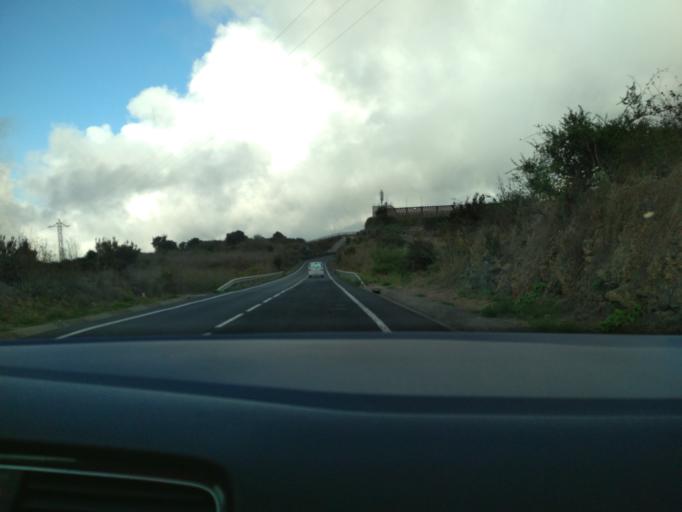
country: ES
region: Canary Islands
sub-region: Provincia de Santa Cruz de Tenerife
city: Santiago del Teide
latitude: 28.3294
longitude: -16.7881
